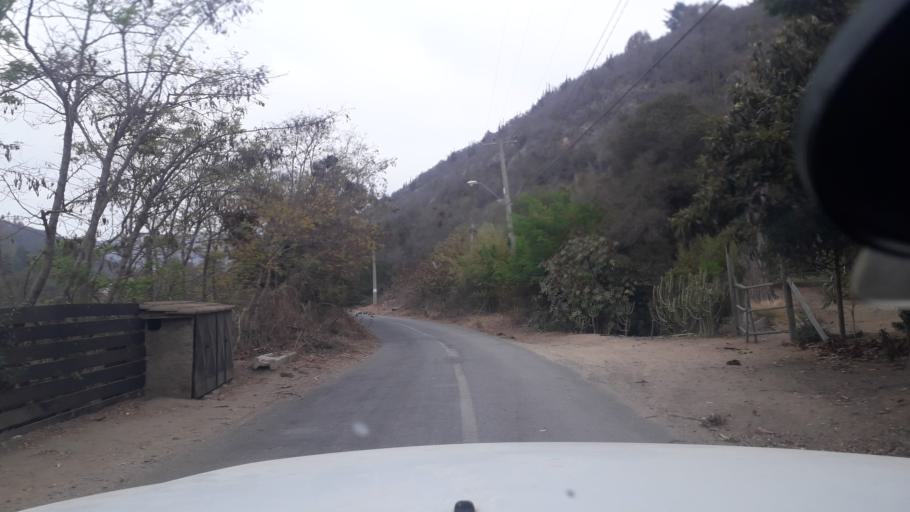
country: CL
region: Valparaiso
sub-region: Provincia de Valparaiso
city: Valparaiso
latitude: -33.1094
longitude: -71.6620
